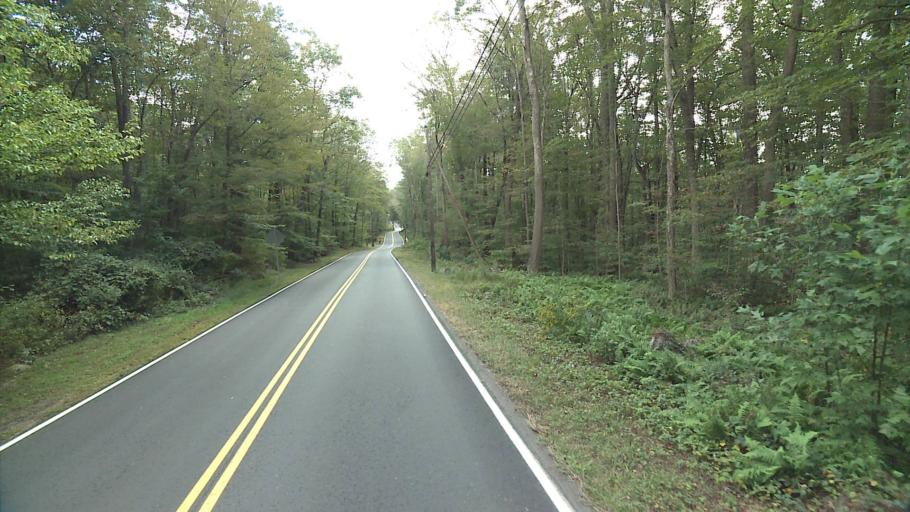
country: US
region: Connecticut
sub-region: New Haven County
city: Madison
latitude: 41.3874
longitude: -72.5960
